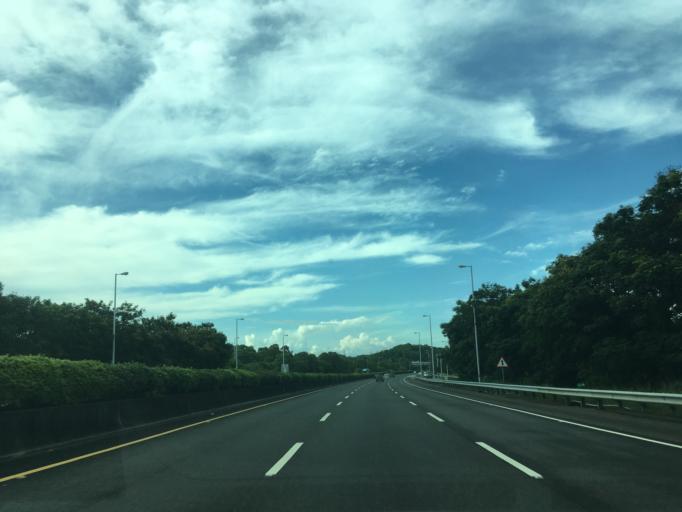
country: TW
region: Taiwan
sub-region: Chiayi
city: Jiayi Shi
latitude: 23.5214
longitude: 120.4848
